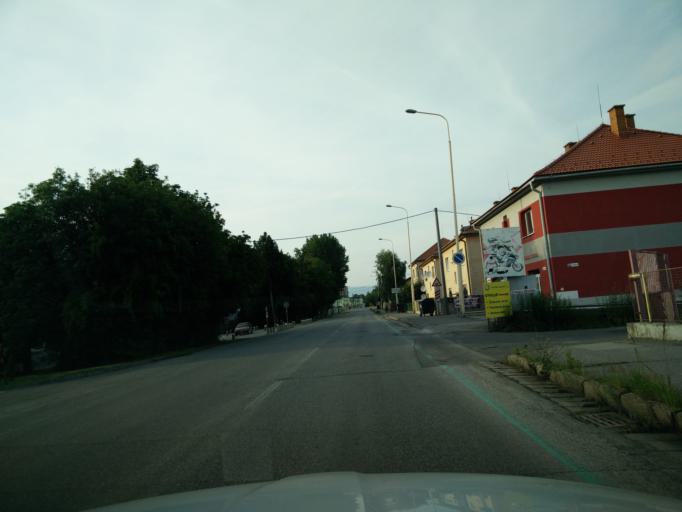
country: SK
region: Nitriansky
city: Prievidza
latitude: 48.7645
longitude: 18.6183
